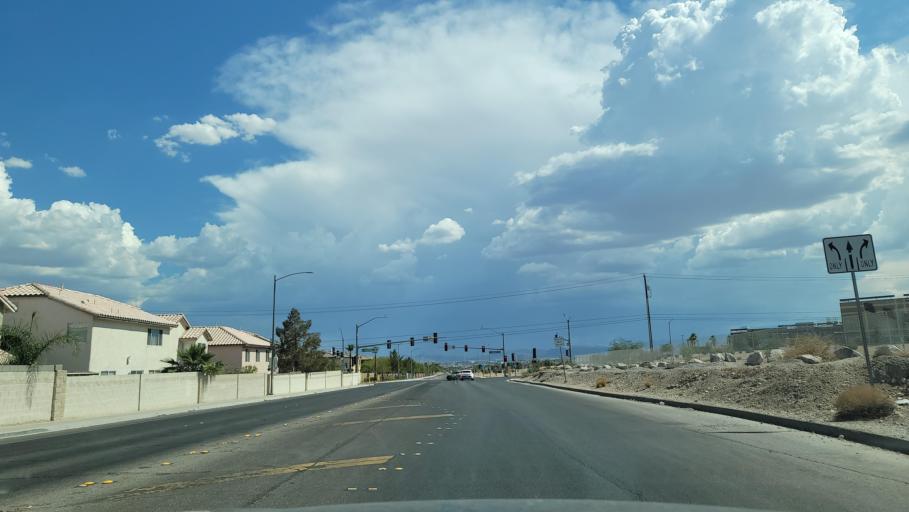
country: US
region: Nevada
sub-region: Clark County
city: Spring Valley
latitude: 36.1269
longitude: -115.2700
